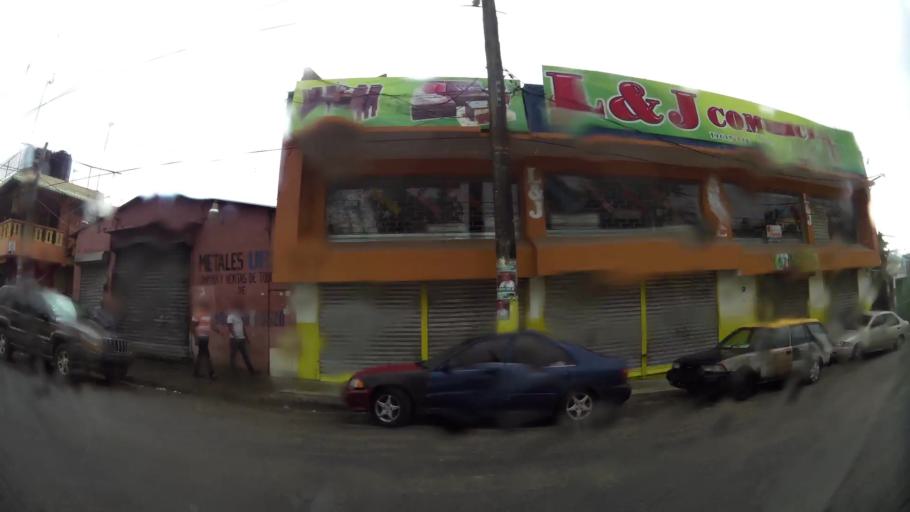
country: DO
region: Nacional
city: La Agustina
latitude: 18.4988
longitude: -69.9293
